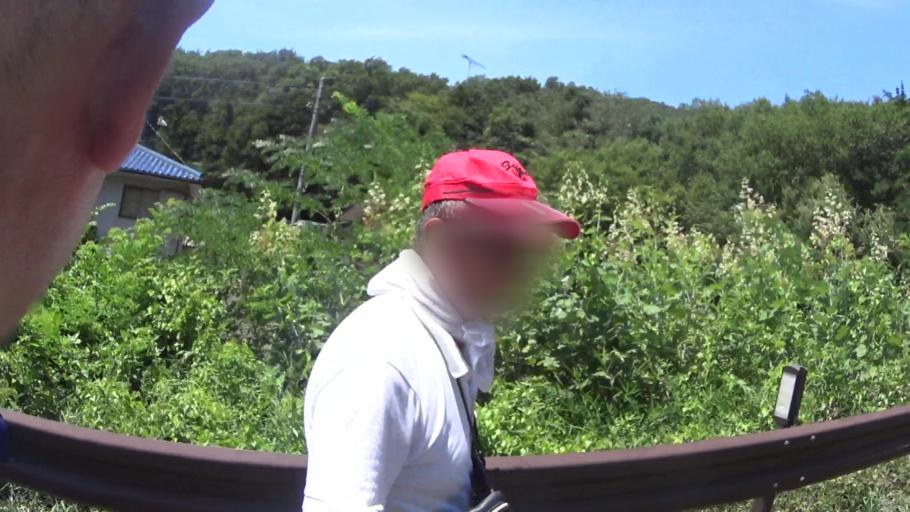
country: JP
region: Gunma
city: Ota
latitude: 36.3108
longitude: 139.3737
